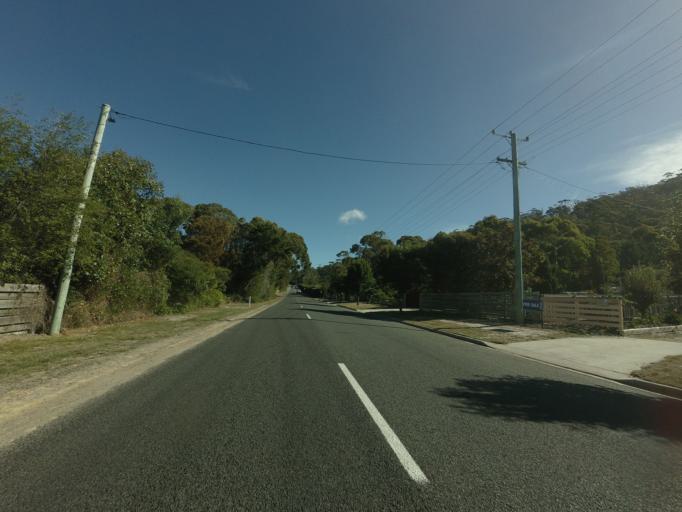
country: AU
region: Tasmania
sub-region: Break O'Day
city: St Helens
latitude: -41.8821
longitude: 148.3012
